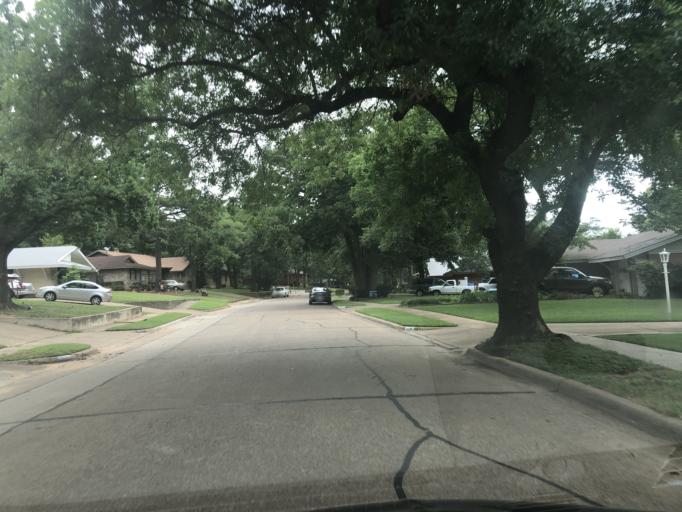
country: US
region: Texas
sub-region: Dallas County
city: Irving
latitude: 32.7981
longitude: -96.9752
